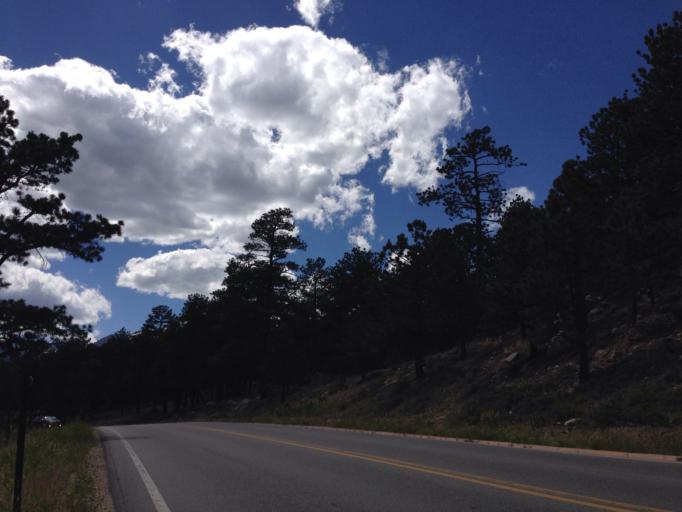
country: US
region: Colorado
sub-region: Larimer County
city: Estes Park
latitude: 40.3606
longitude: -105.5891
